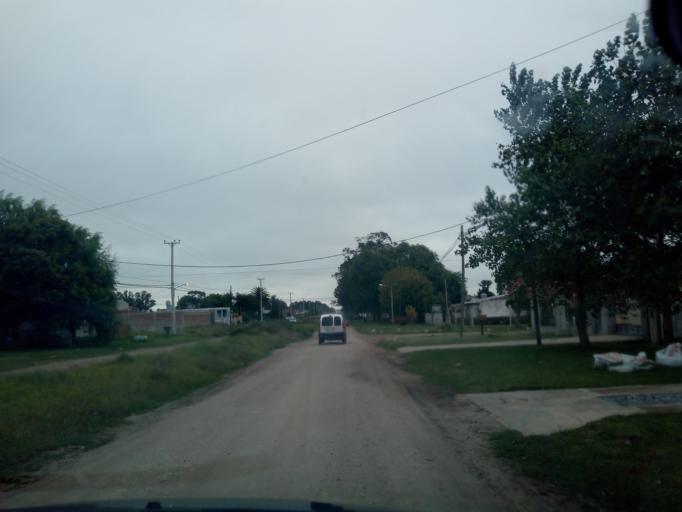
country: AR
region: Buenos Aires
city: Mar del Plata
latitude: -38.0679
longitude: -57.5700
